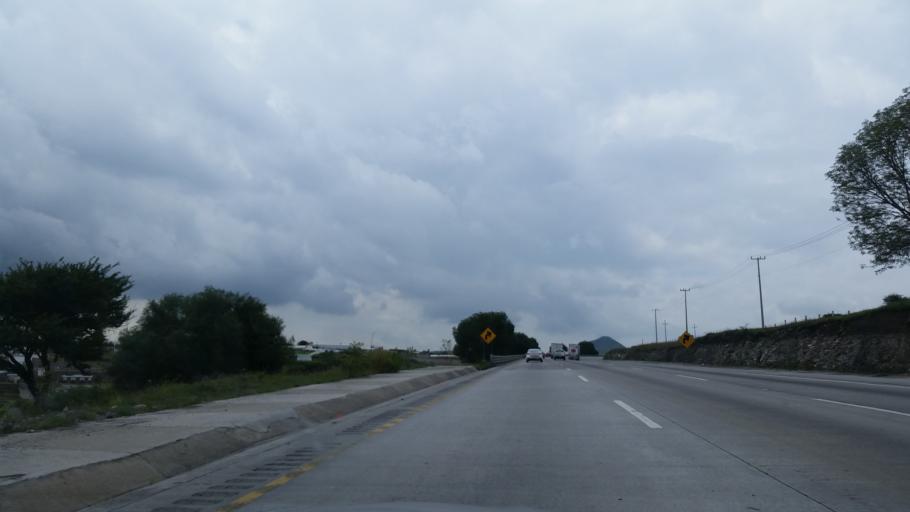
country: MX
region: Hidalgo
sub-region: Tepeji del Rio de Ocampo
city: Cantera de Villagran
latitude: 19.8575
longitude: -99.3036
